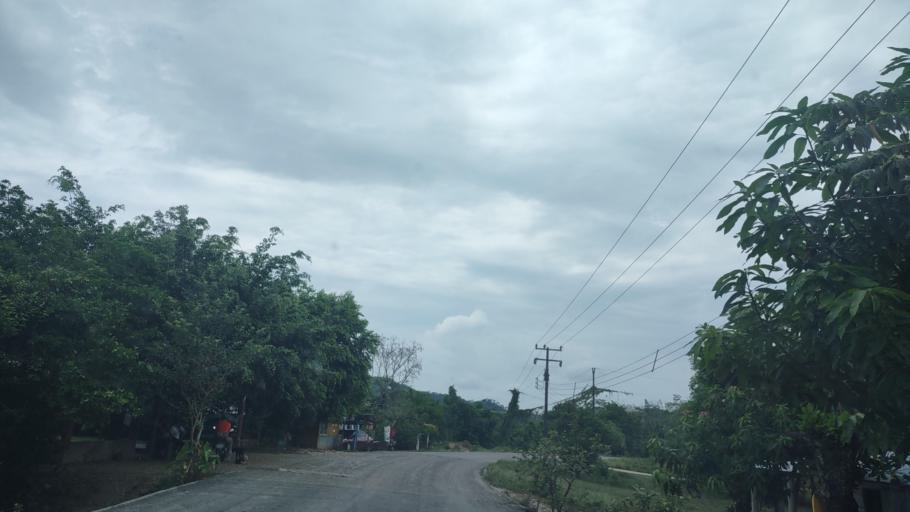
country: MX
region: Tabasco
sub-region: Huimanguillo
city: Francisco Rueda
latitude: 17.5306
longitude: -94.1275
